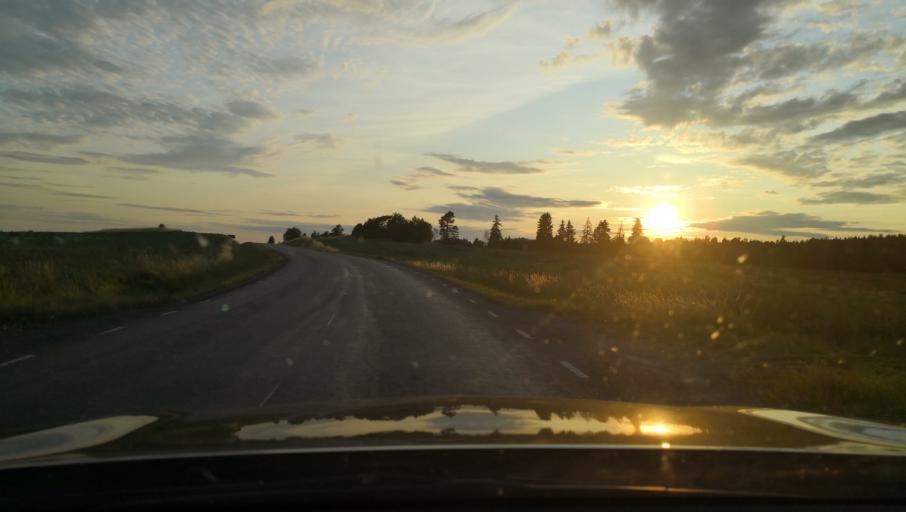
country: SE
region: Uppsala
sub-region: Uppsala Kommun
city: Vattholma
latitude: 60.0176
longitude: 17.7149
